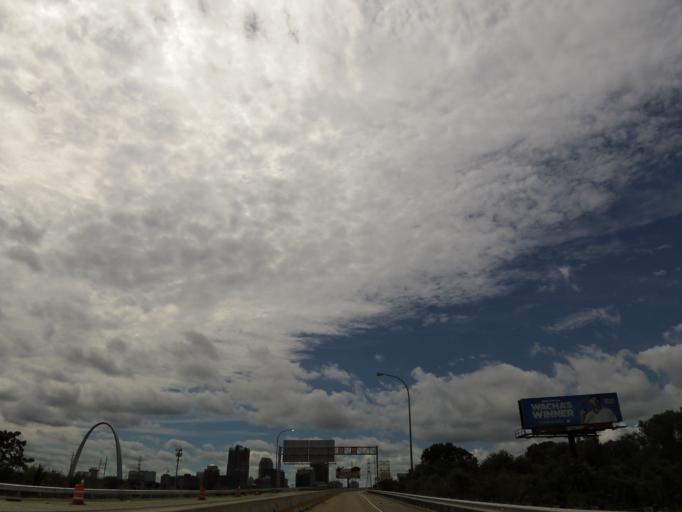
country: US
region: Illinois
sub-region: Saint Clair County
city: East Saint Louis
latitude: 38.6301
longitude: -90.1691
